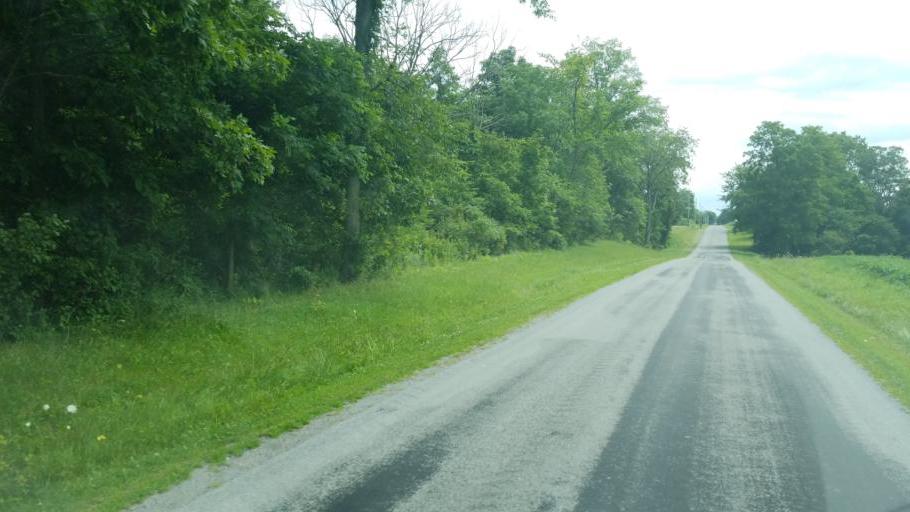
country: US
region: Ohio
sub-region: Wyandot County
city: Upper Sandusky
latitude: 40.8770
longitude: -83.1620
